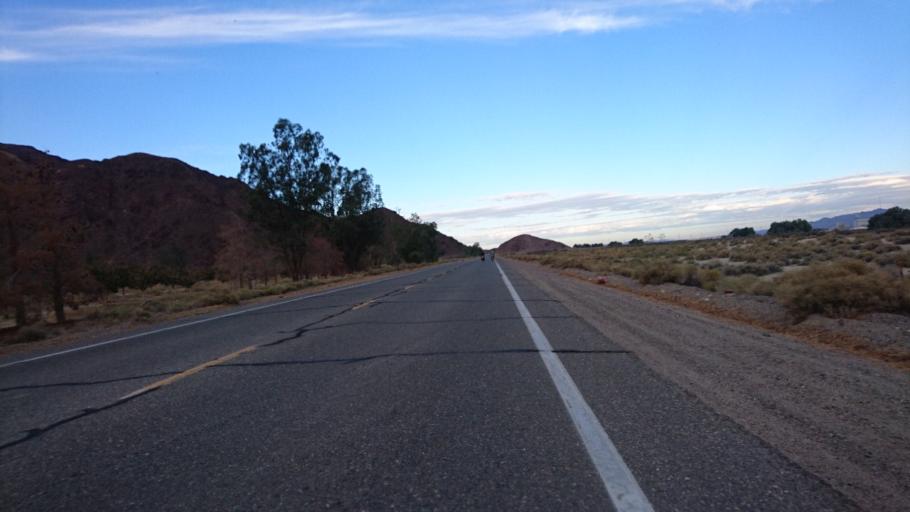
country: US
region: California
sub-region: San Bernardino County
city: Barstow
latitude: 34.8241
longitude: -116.6694
